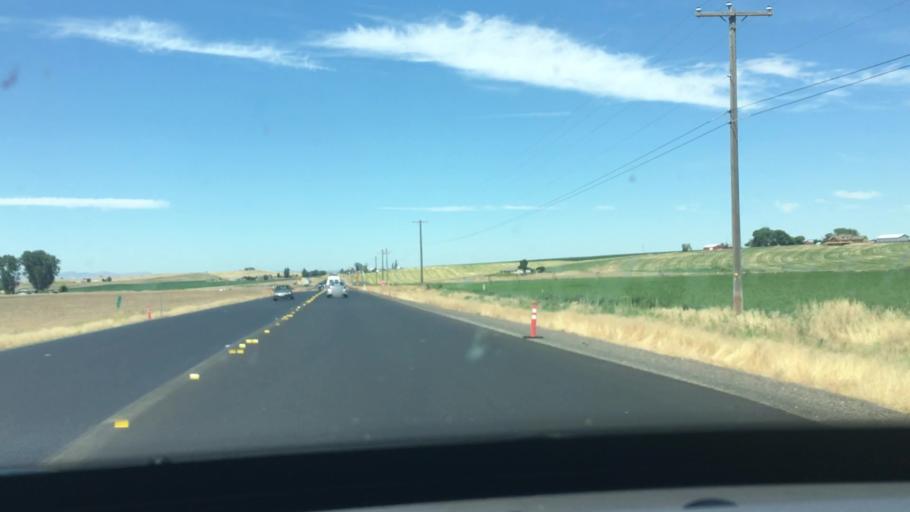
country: US
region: Oregon
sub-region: Jefferson County
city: Culver
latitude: 44.5141
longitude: -121.1845
